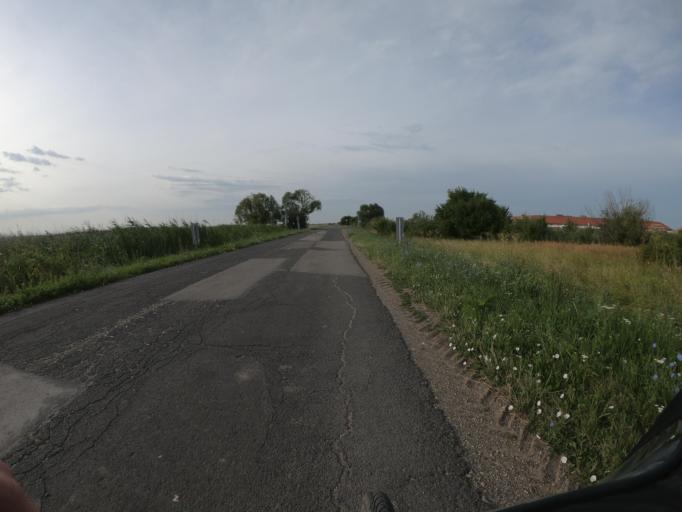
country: HU
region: Hajdu-Bihar
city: Hortobagy
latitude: 47.6028
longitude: 21.0760
